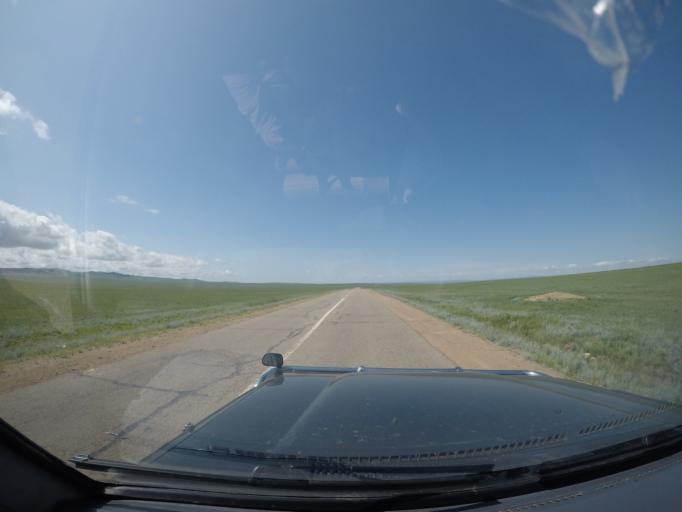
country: MN
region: Hentiy
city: Bayan
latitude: 47.2838
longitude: 110.9259
